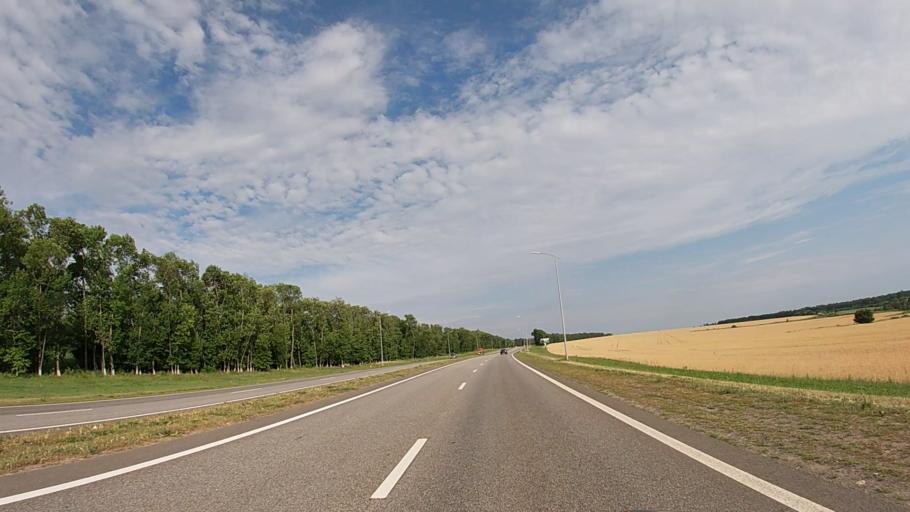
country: RU
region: Belgorod
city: Tomarovka
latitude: 50.6687
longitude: 36.3069
